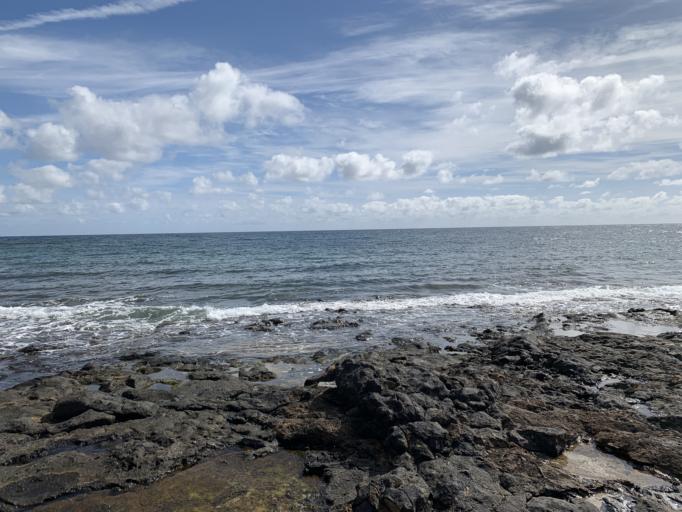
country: ES
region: Canary Islands
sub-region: Provincia de Las Palmas
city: Puerto del Rosario
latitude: 28.5014
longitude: -13.8470
